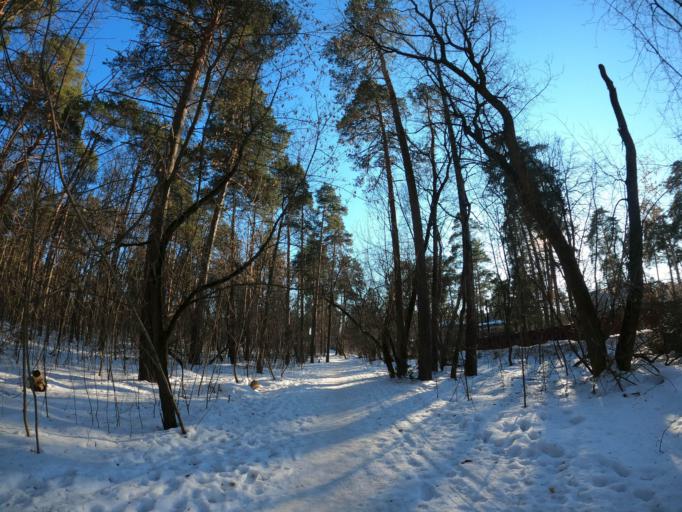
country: RU
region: Moskovskaya
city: Udel'naya
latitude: 55.6382
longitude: 37.9989
